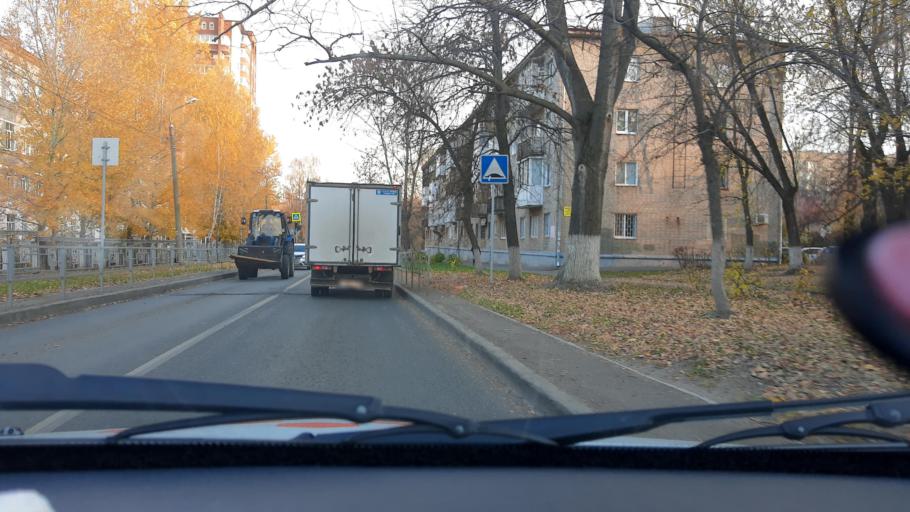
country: RU
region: Bashkortostan
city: Ufa
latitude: 54.7874
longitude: 56.0295
